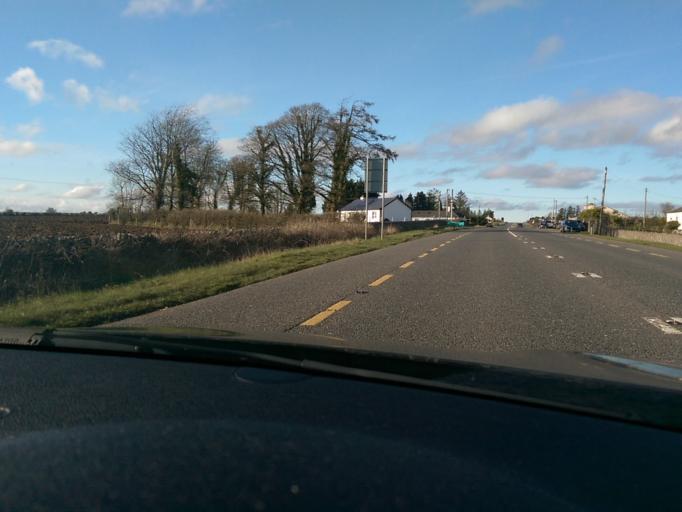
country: IE
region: Connaught
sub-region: Roscommon
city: Roscommon
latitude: 53.6635
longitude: -8.1982
